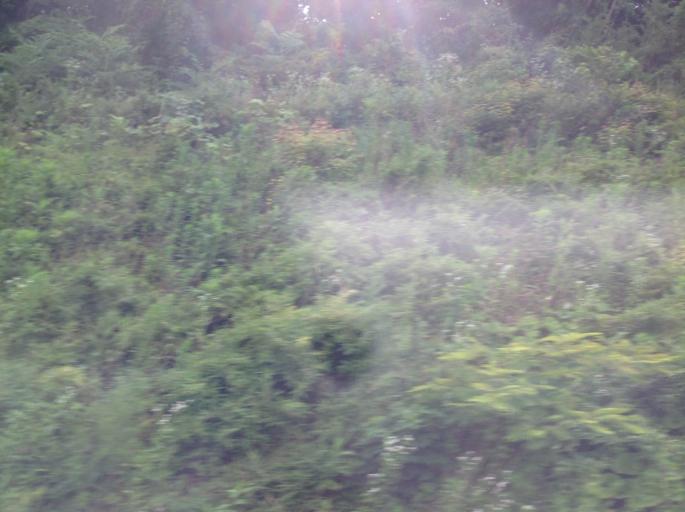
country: JP
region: Miyagi
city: Tomiya
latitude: 38.3749
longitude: 140.8879
